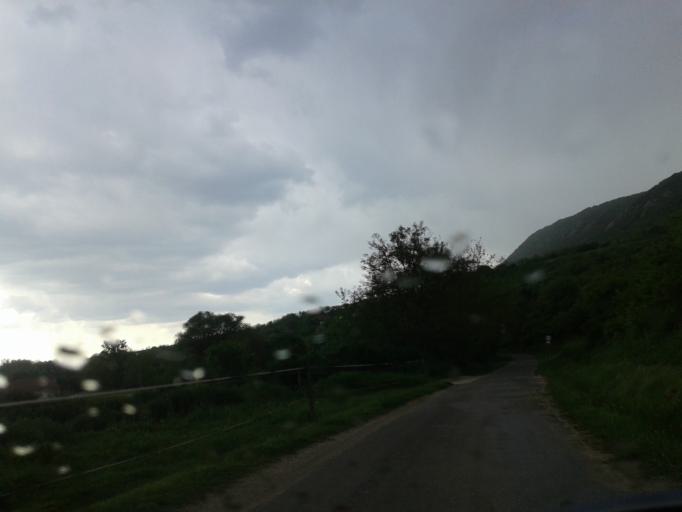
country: HU
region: Komarom-Esztergom
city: Kesztolc
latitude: 47.7124
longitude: 18.8146
